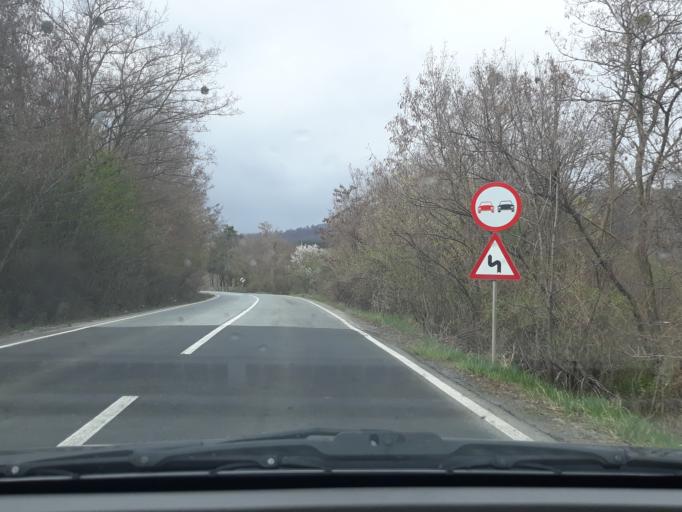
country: RO
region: Harghita
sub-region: Comuna Lupeni
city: Lupeni
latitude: 46.4028
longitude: 25.2152
